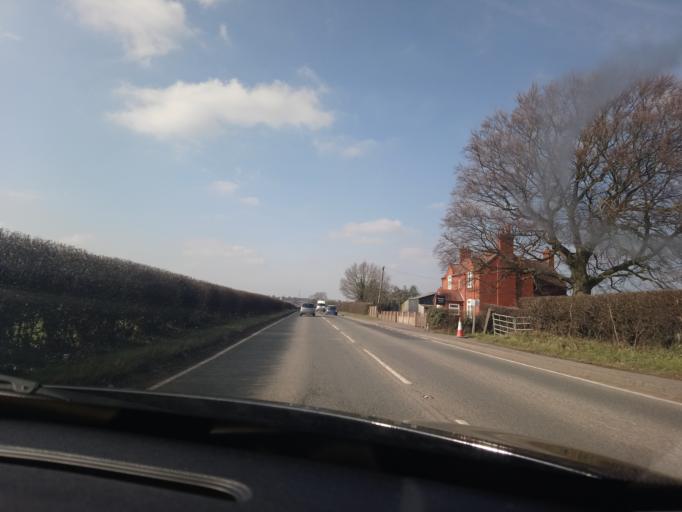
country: GB
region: England
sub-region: Shropshire
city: Berrington
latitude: 52.6869
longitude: -2.6973
